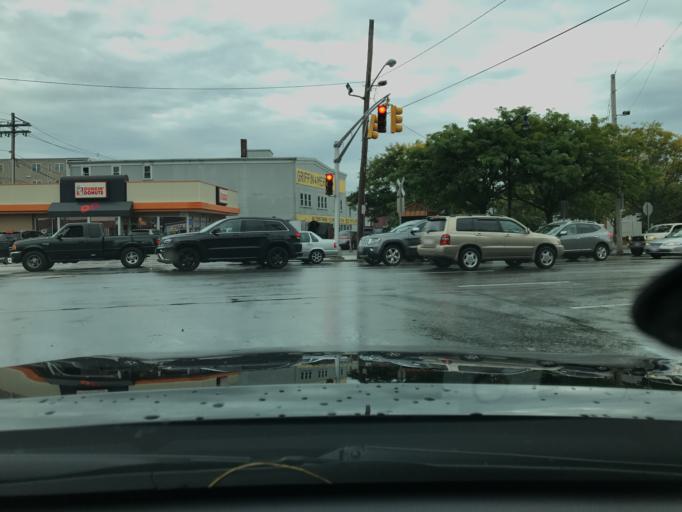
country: US
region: Massachusetts
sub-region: Essex County
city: Peabody
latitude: 42.5269
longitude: -70.9275
